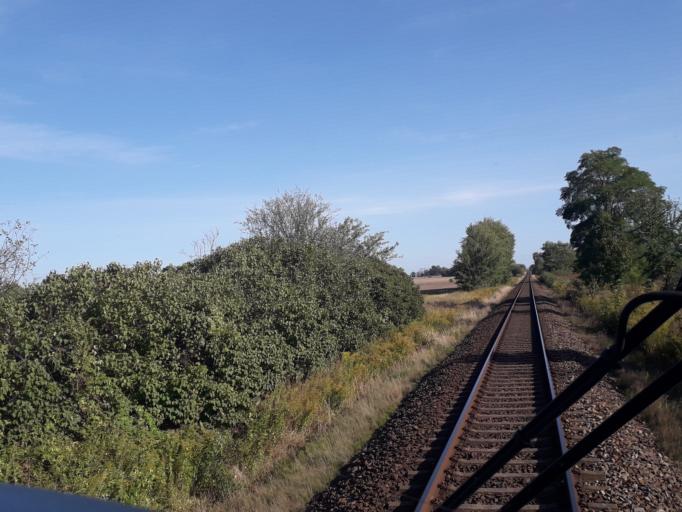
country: DE
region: Brandenburg
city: Kremmen
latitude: 52.7343
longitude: 13.0926
